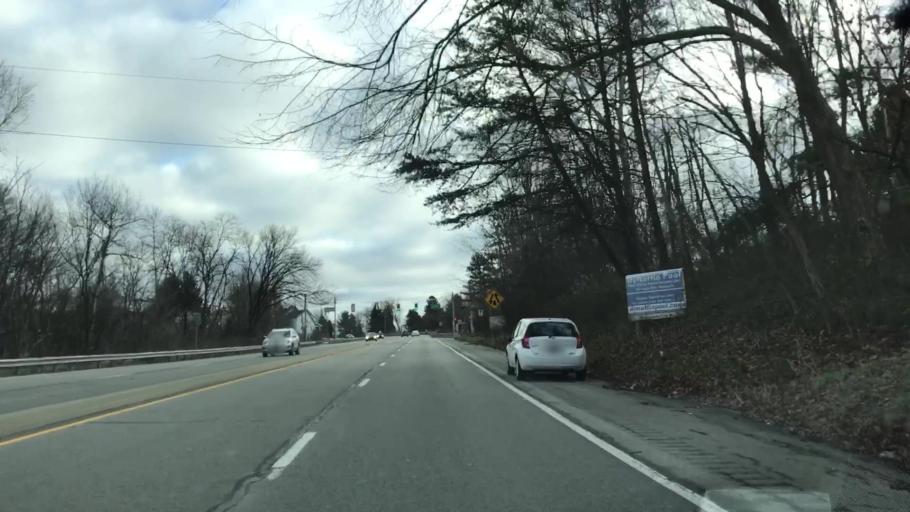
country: US
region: Pennsylvania
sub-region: Beaver County
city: Aliquippa
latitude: 40.6022
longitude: -80.2944
